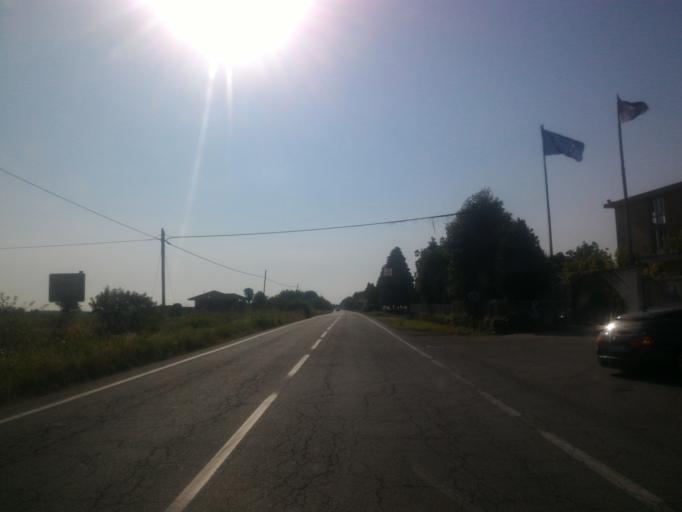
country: IT
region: Piedmont
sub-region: Provincia di Torino
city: Buriasco
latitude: 44.8754
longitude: 7.3931
